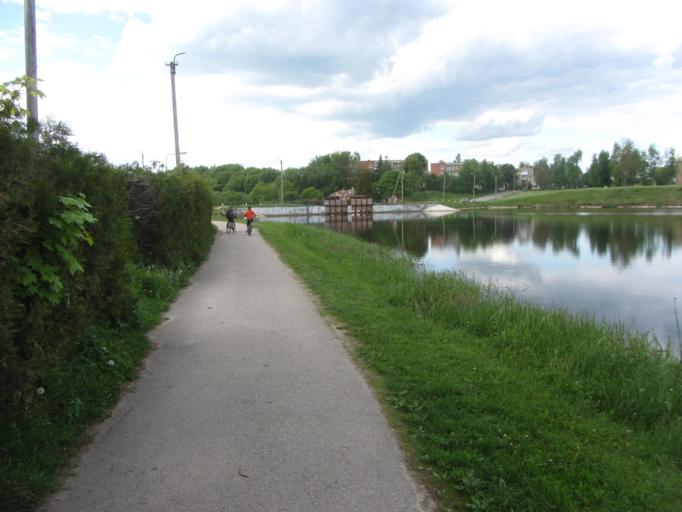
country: LT
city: Sirvintos
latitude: 55.0457
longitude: 24.9549
